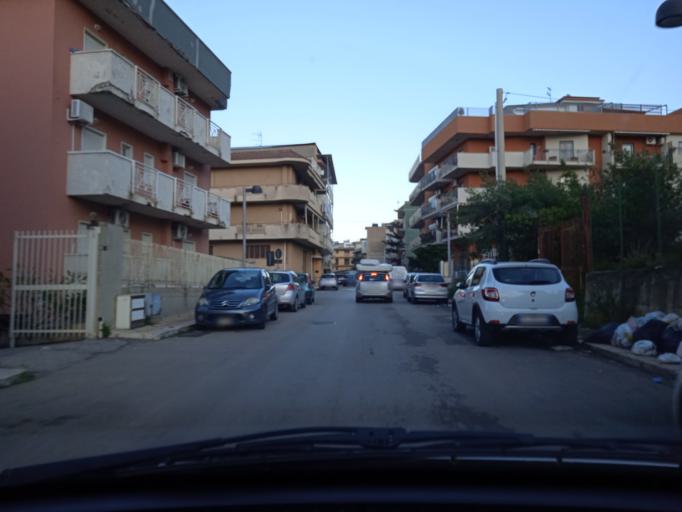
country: IT
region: Sicily
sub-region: Palermo
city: Villabate
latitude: 38.0739
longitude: 13.4448
